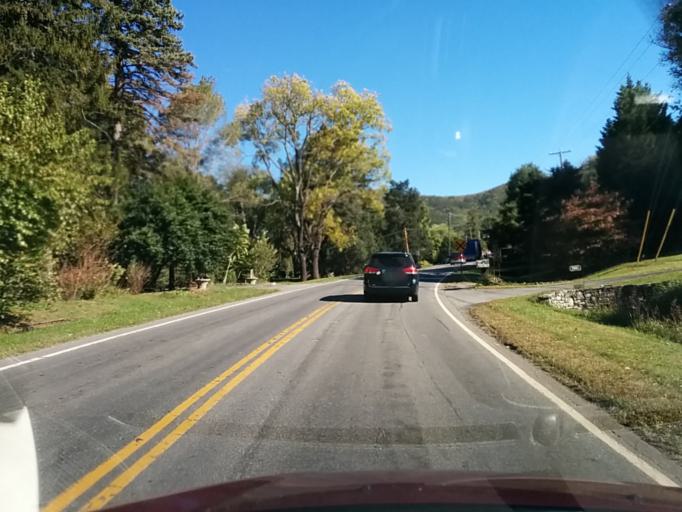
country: US
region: Virginia
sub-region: Roanoke County
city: Hollins
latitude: 37.3504
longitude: -79.9236
